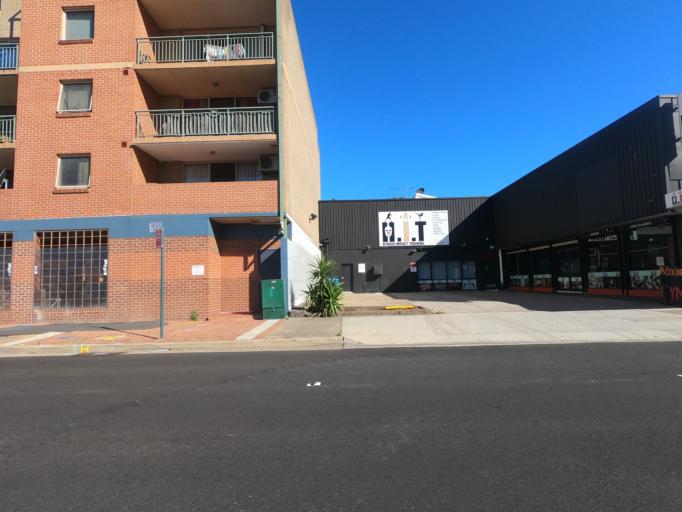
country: AU
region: New South Wales
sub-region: Fairfield
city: Liverpool
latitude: -33.9267
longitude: 150.9216
